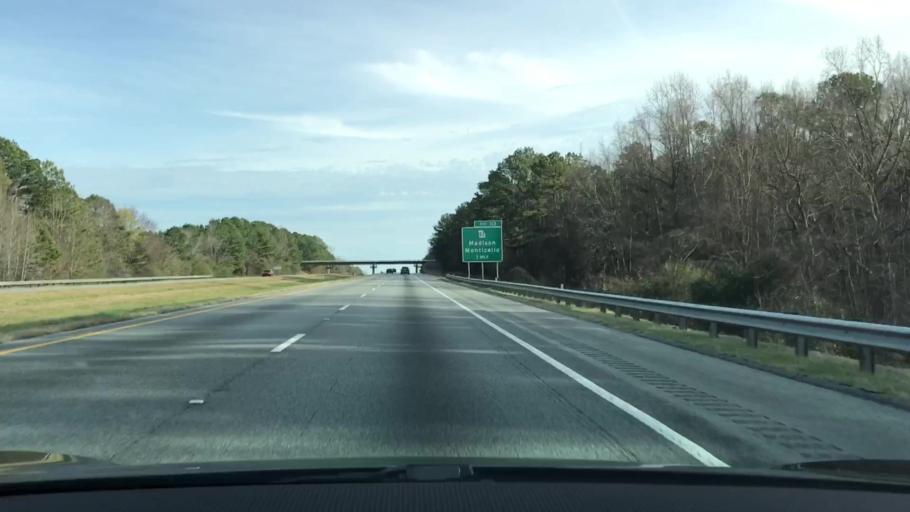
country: US
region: Georgia
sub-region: Morgan County
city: Madison
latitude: 33.5700
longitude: -83.5184
